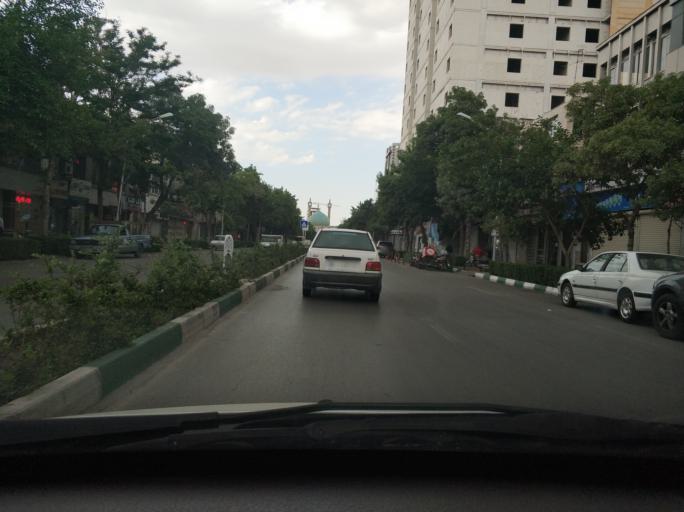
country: IR
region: Razavi Khorasan
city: Mashhad
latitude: 36.2879
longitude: 59.6040
